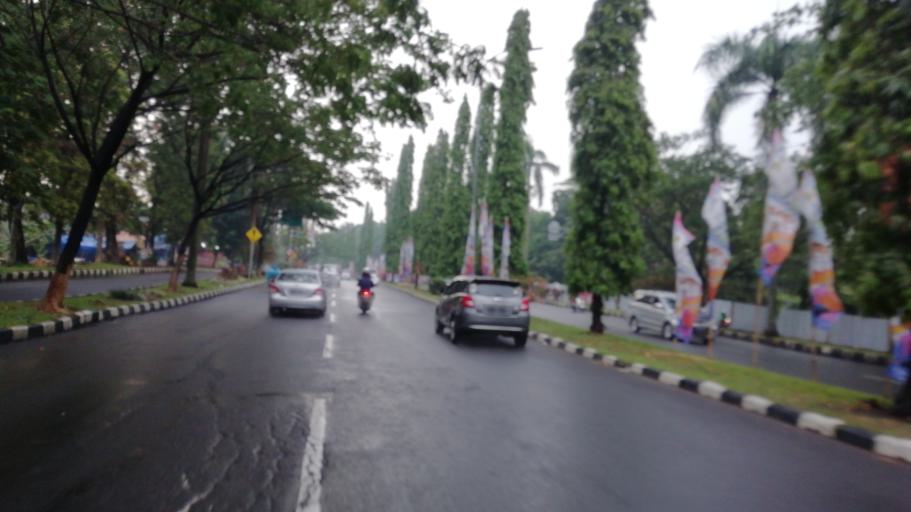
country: ID
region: West Java
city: Cibinong
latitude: -6.4819
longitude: 106.8300
